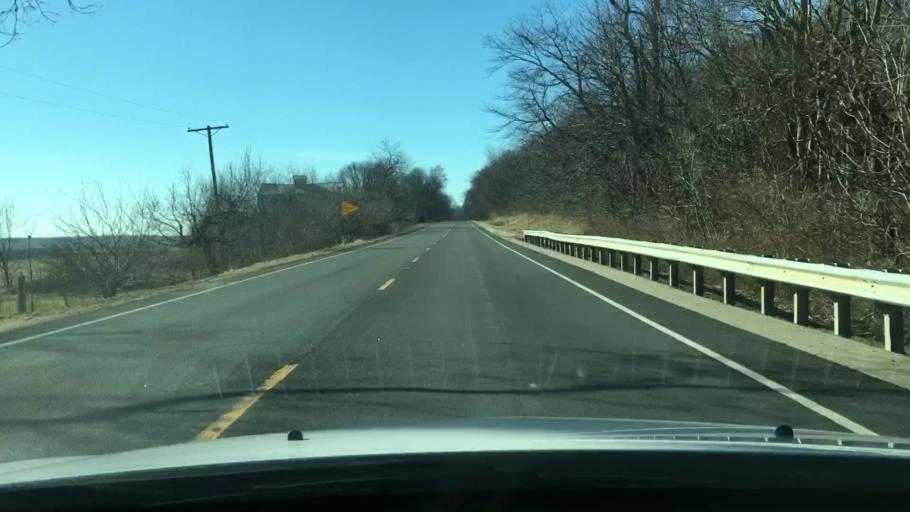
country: US
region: Illinois
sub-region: Mason County
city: Havana
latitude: 40.4149
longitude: -90.0156
